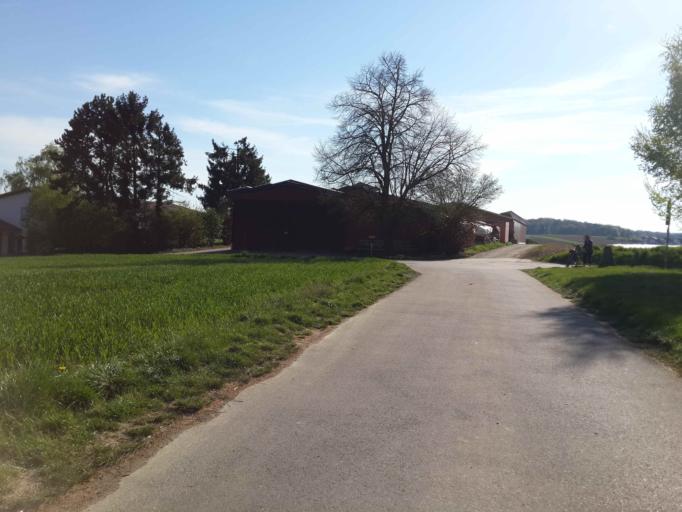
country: DE
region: Baden-Wuerttemberg
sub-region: Regierungsbezirk Stuttgart
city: Massenbachhausen
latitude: 49.1742
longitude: 9.0571
